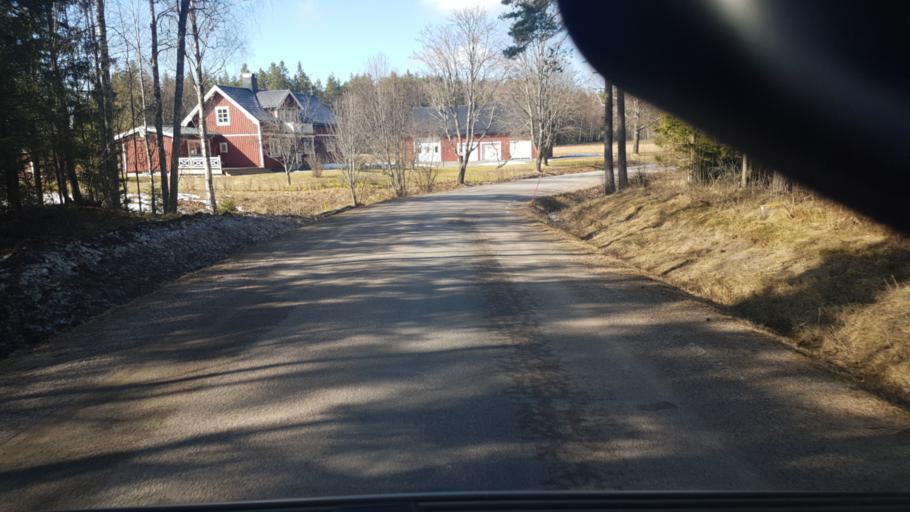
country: SE
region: Vaermland
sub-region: Eda Kommun
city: Charlottenberg
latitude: 59.8596
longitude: 12.3441
